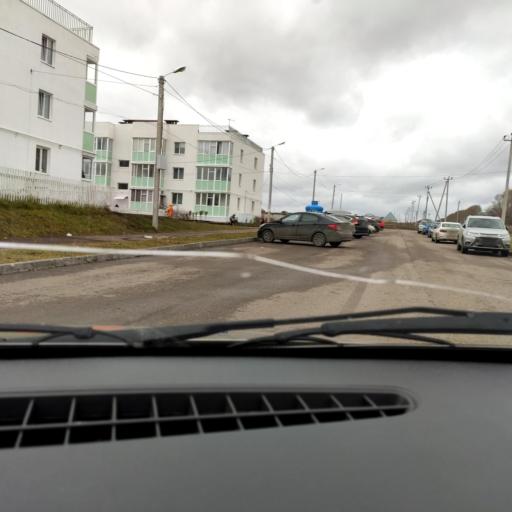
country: RU
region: Bashkortostan
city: Kabakovo
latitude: 54.4658
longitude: 55.9526
